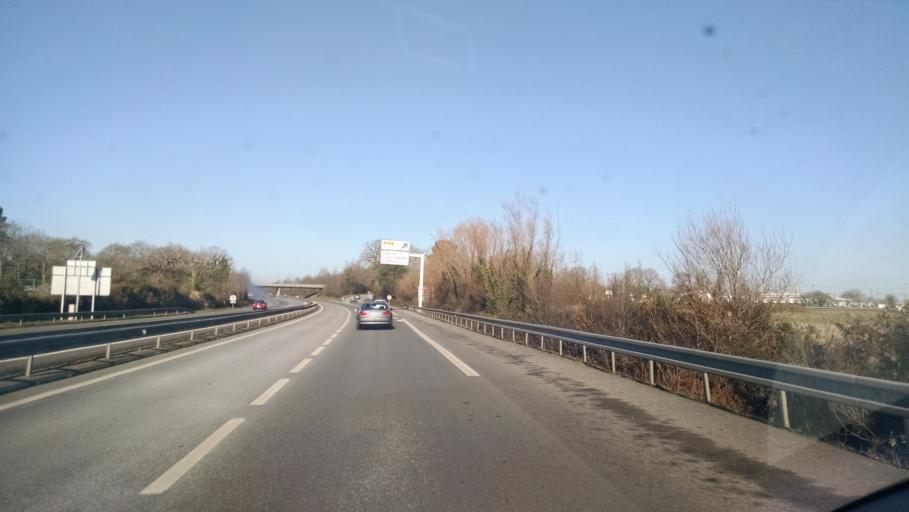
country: FR
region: Brittany
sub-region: Departement du Morbihan
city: Auray
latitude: 47.6801
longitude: -3.0196
